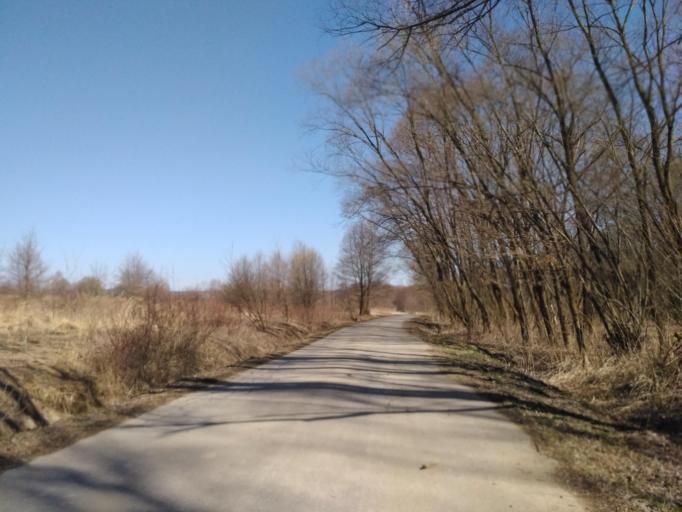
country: PL
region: Subcarpathian Voivodeship
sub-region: Powiat brzozowski
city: Orzechowka
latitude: 49.7100
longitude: 21.9666
